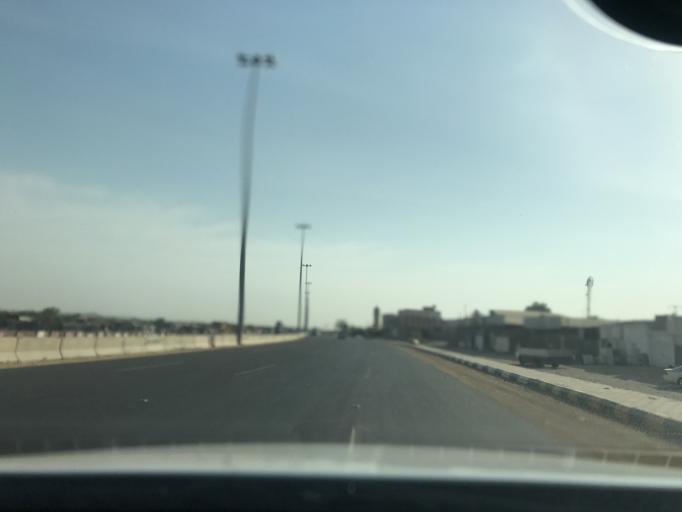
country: SA
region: Makkah
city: Al Jumum
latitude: 21.4383
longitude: 39.5240
